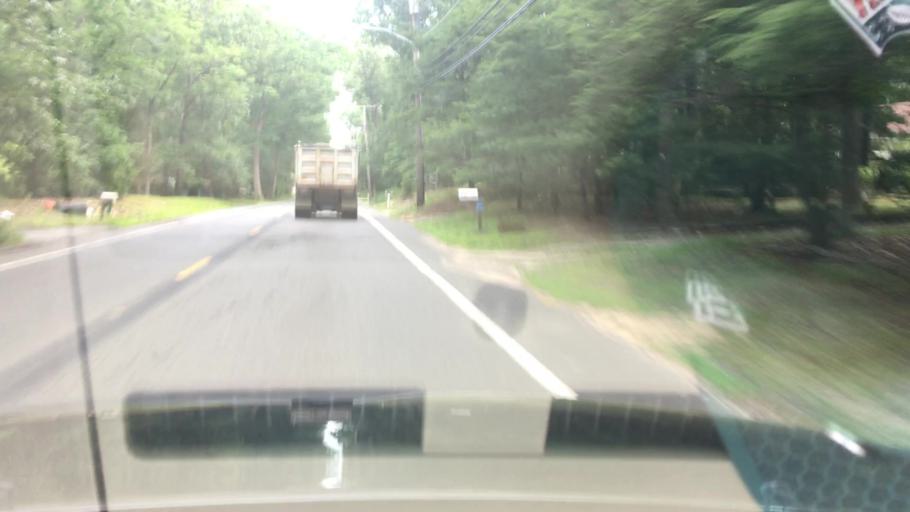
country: US
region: New Jersey
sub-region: Ocean County
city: Vista Center
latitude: 40.1163
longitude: -74.3915
